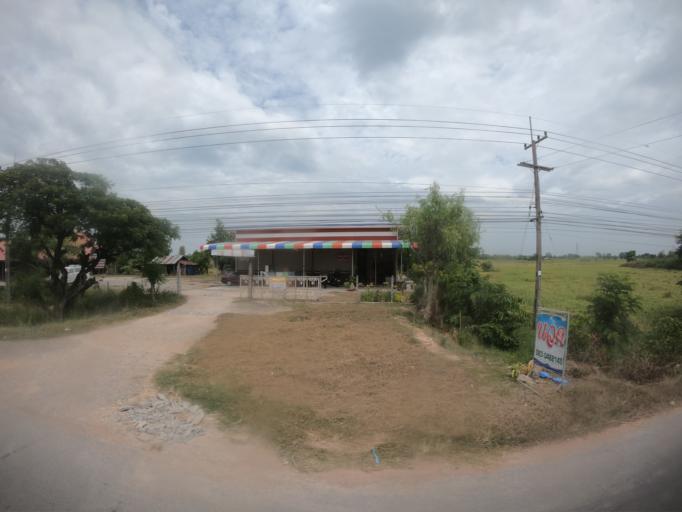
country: TH
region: Maha Sarakham
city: Maha Sarakham
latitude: 16.1594
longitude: 103.3593
